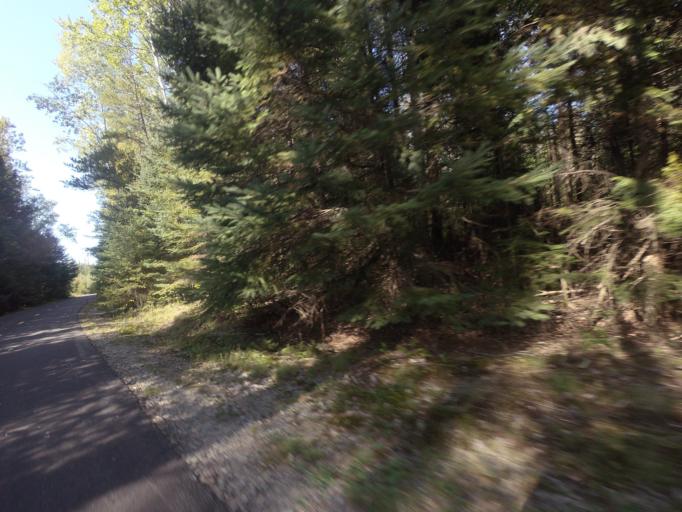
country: CA
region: Quebec
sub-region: Laurentides
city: Mont-Tremblant
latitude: 46.1242
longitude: -74.5431
